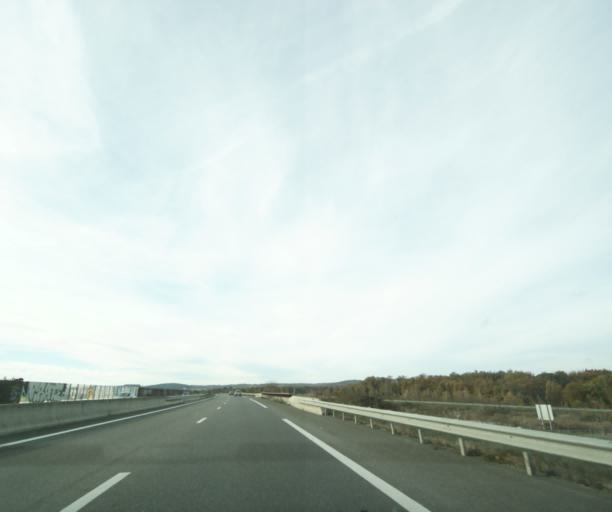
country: FR
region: Midi-Pyrenees
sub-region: Departement de la Haute-Garonne
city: Leguevin
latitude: 43.5819
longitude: 1.2186
